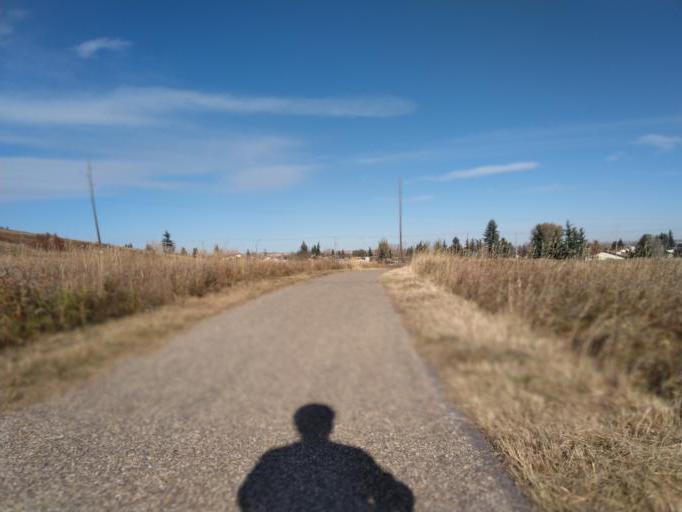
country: CA
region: Alberta
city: Calgary
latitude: 51.1237
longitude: -114.0987
